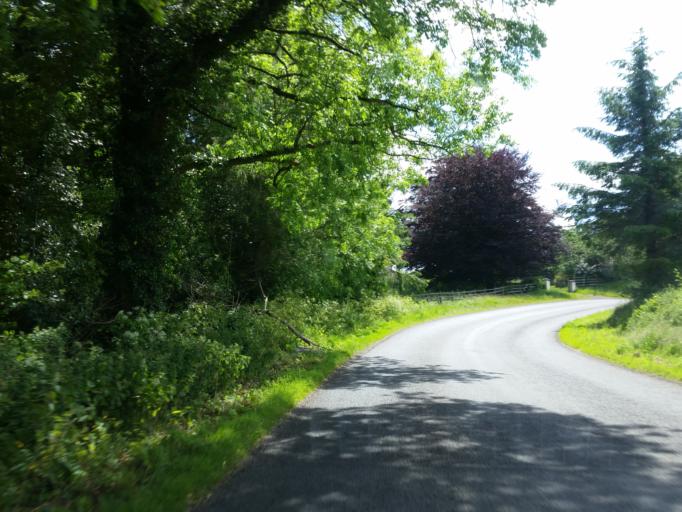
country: GB
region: Northern Ireland
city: Fivemiletown
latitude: 54.3688
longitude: -7.3094
